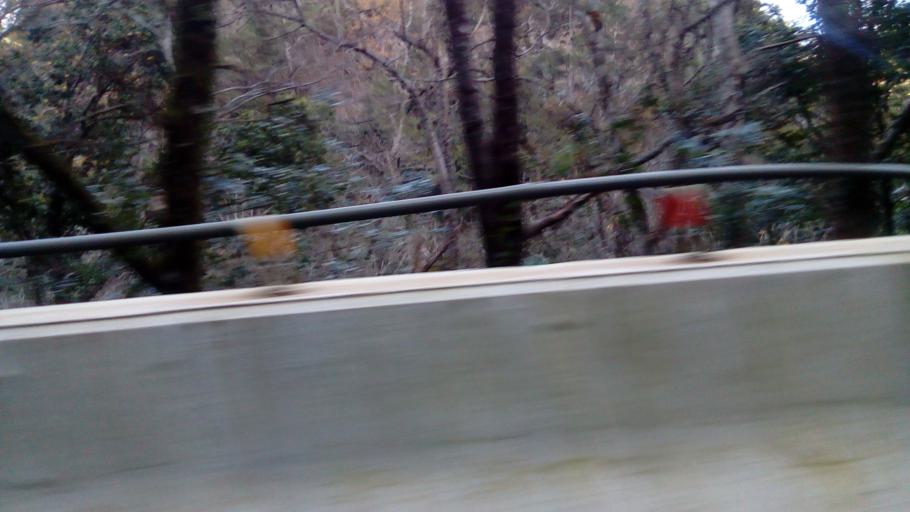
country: TW
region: Taiwan
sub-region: Hualien
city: Hualian
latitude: 24.3432
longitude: 121.3110
